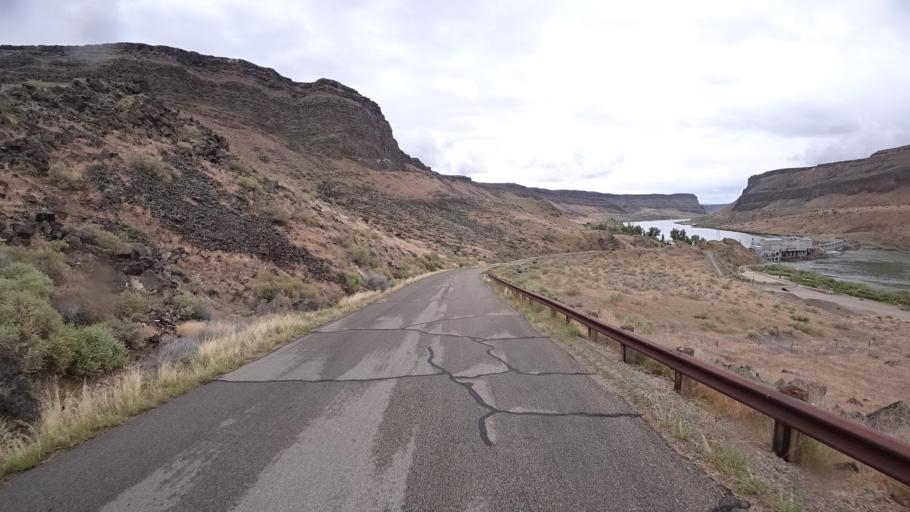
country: US
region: Idaho
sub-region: Owyhee County
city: Murphy
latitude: 43.2486
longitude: -116.3769
